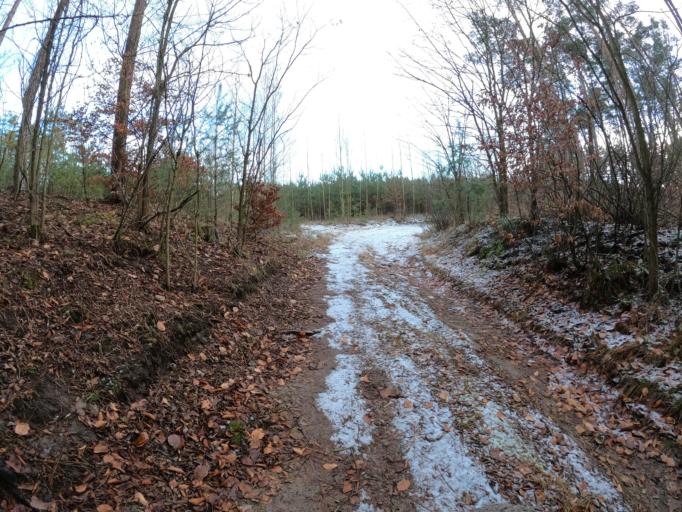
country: PL
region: Lubusz
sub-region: Powiat slubicki
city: Cybinka
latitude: 52.2195
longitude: 14.8365
